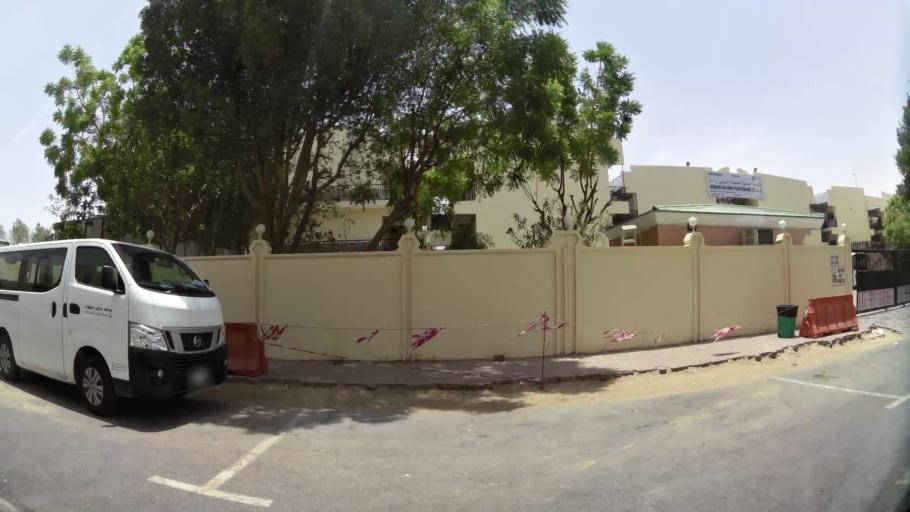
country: AE
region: Ash Shariqah
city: Sharjah
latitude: 25.2687
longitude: 55.4315
